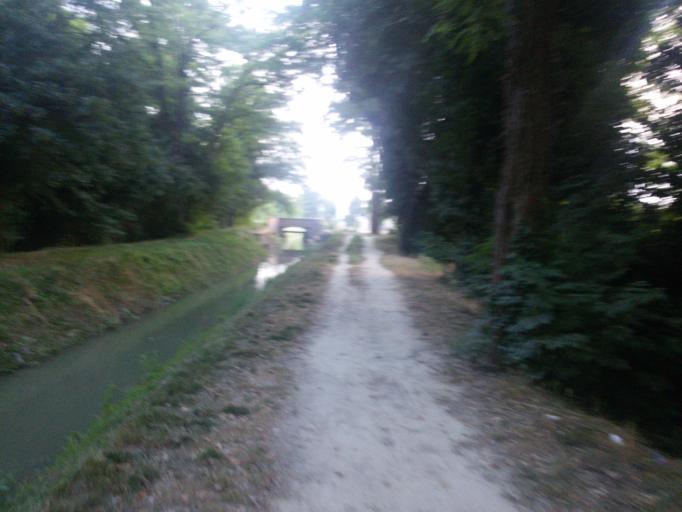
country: IT
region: Emilia-Romagna
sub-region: Provincia di Ravenna
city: Lugo
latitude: 44.4191
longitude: 11.8995
